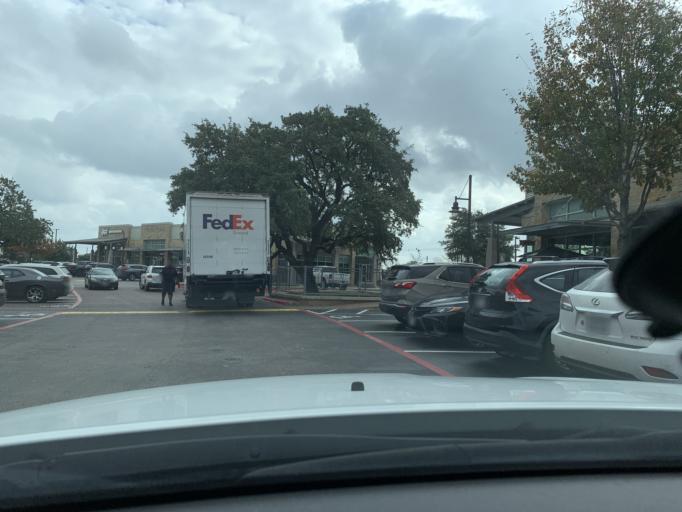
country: US
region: Texas
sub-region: Williamson County
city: Round Rock
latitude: 30.5604
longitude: -97.6906
